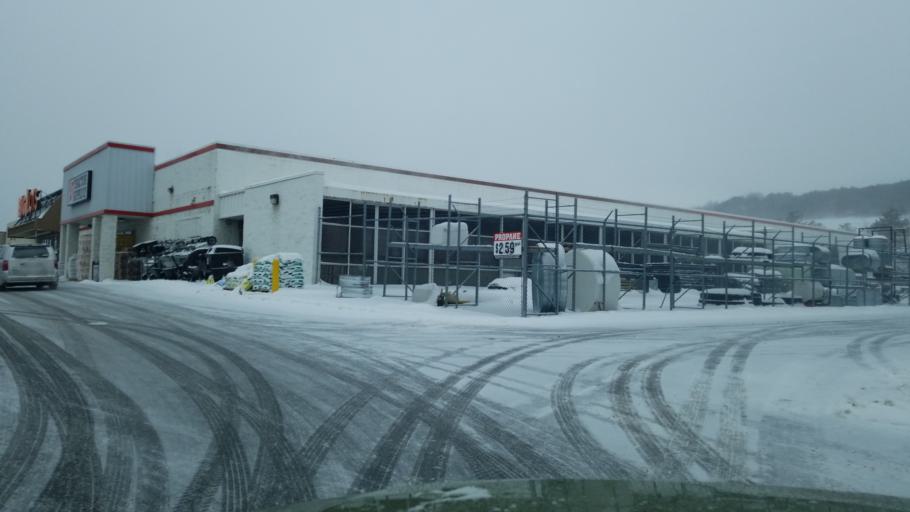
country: US
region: Pennsylvania
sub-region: Clearfield County
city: Clearfield
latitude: 41.0292
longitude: -78.4122
